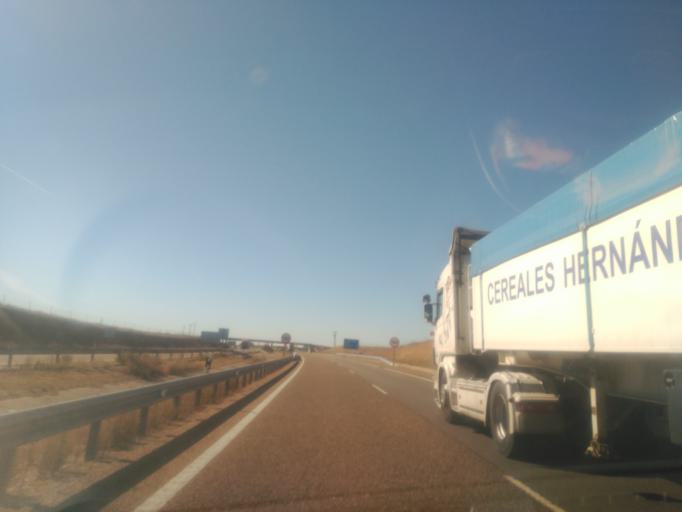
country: ES
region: Castille and Leon
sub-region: Provincia de Valladolid
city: Siete Iglesias de Trabancos
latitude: 41.3414
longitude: -5.1841
